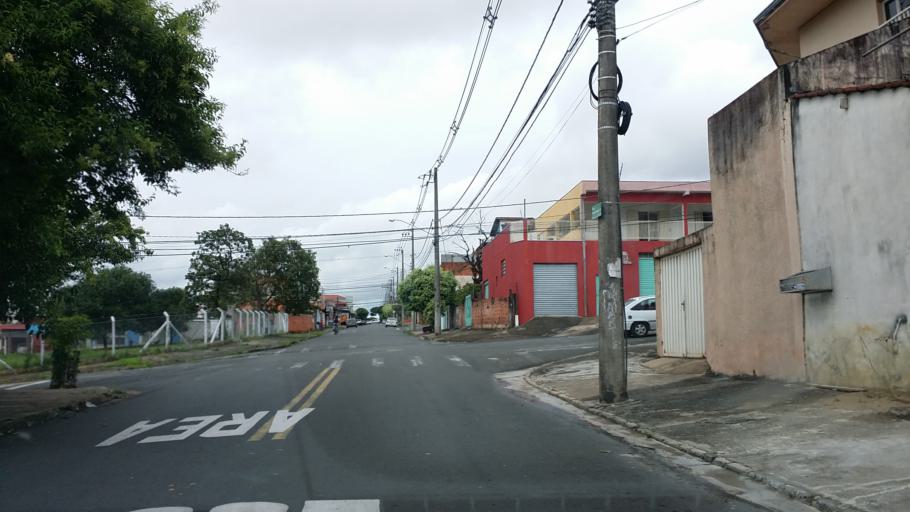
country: BR
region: Sao Paulo
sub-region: Indaiatuba
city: Indaiatuba
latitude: -23.1253
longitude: -47.2308
